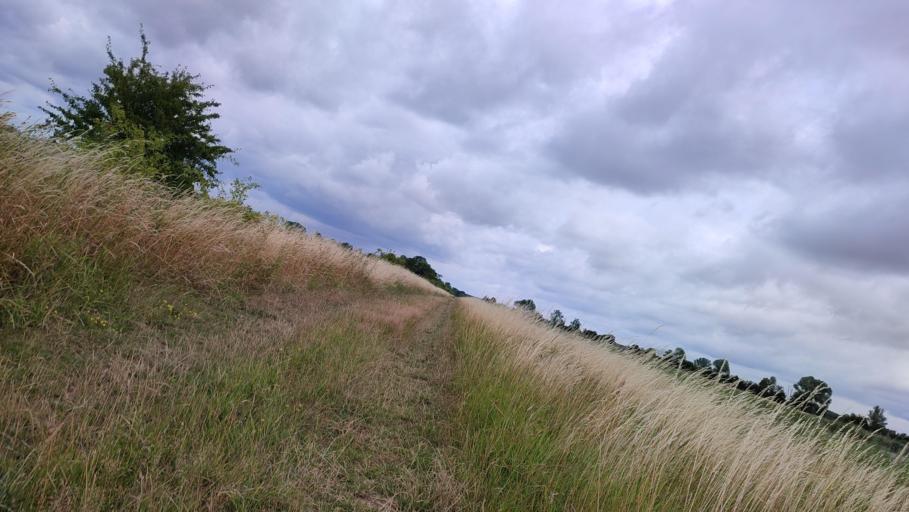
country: DE
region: Lower Saxony
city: Hitzacker
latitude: 53.1624
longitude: 11.1032
